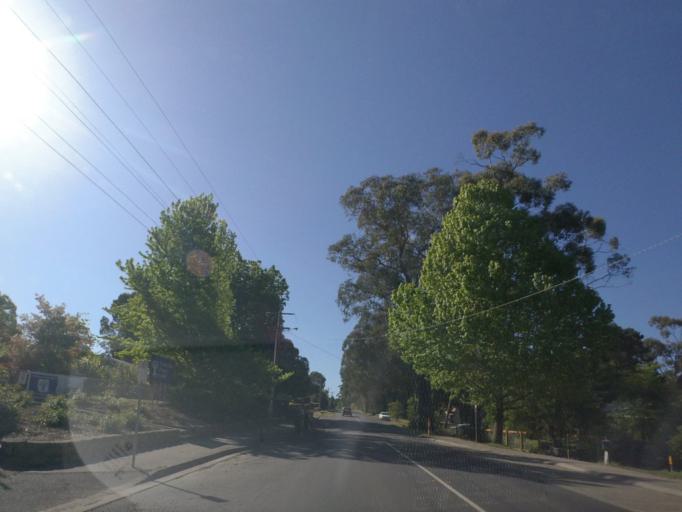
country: AU
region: Victoria
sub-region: Yarra Ranges
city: Yarra Junction
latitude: -37.8204
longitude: 145.6513
